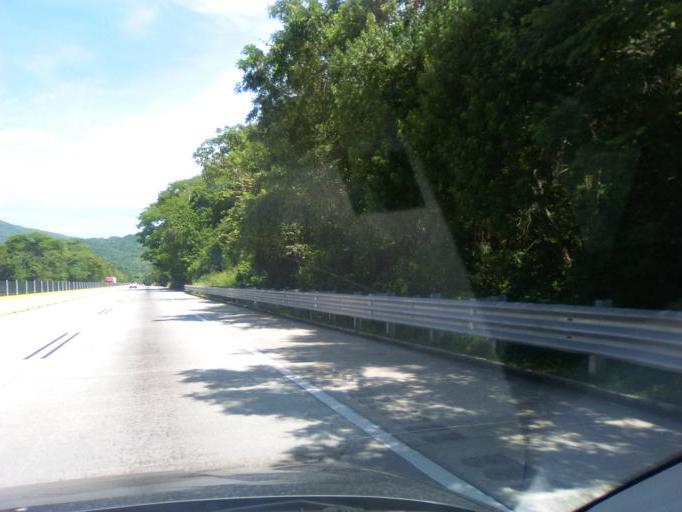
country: MX
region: Guerrero
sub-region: Acapulco de Juarez
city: Kilometro 30
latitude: 16.9835
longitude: -99.7088
